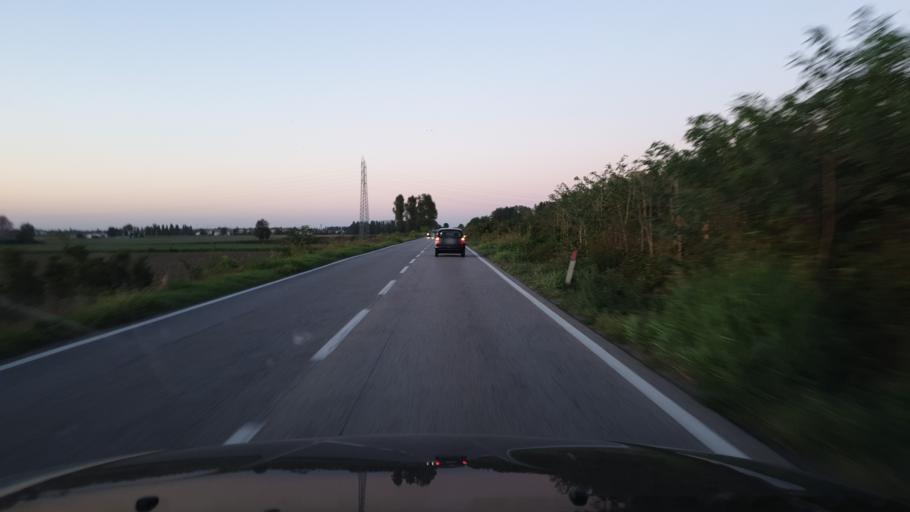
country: IT
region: Emilia-Romagna
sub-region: Provincia di Bologna
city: Minerbio
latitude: 44.6441
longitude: 11.4769
